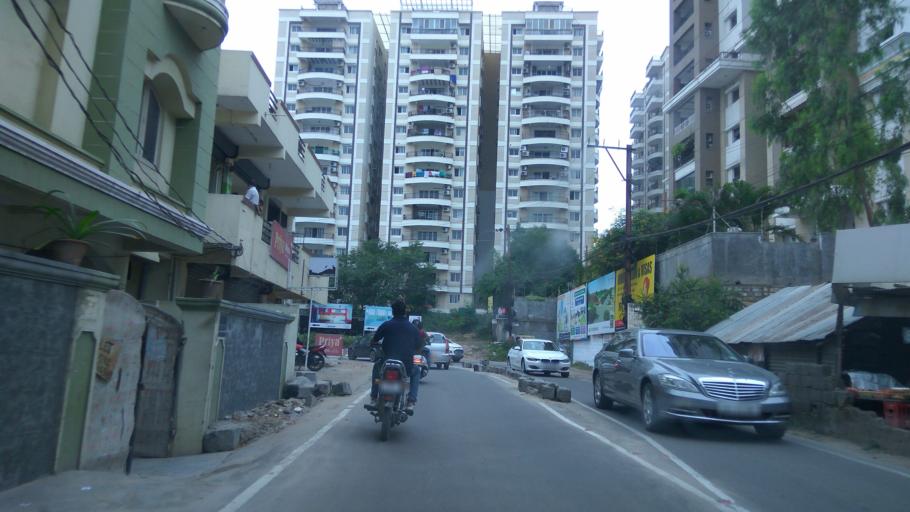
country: IN
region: Telangana
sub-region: Rangareddi
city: Kukatpalli
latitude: 17.4386
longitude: 78.3906
